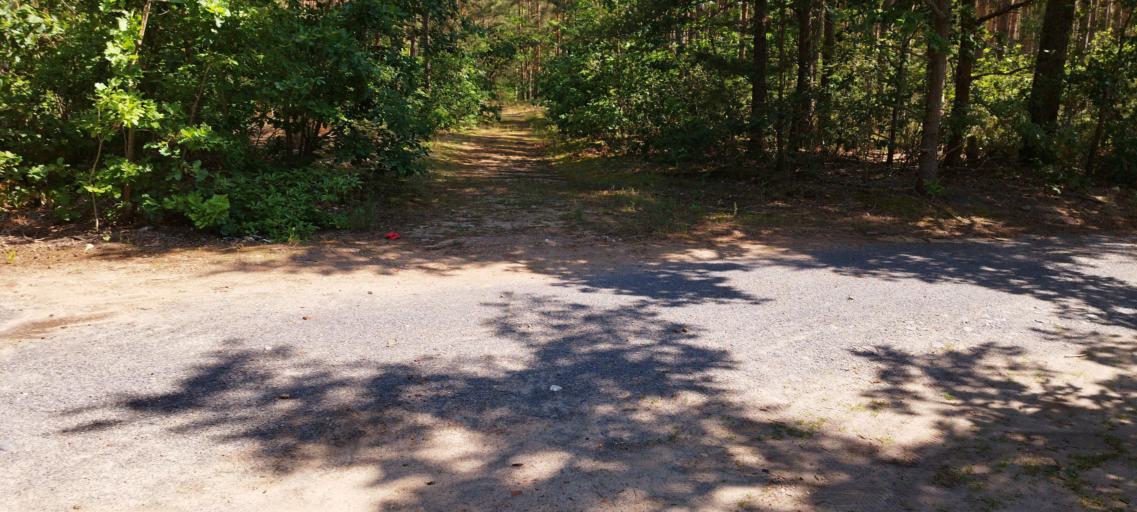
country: DE
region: Brandenburg
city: Bad Saarow
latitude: 52.3015
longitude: 14.0586
